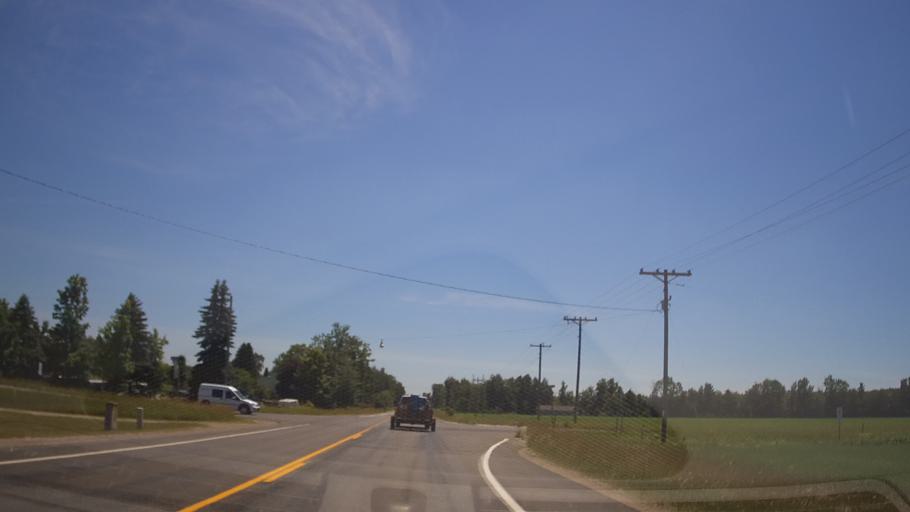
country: US
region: Michigan
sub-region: Grand Traverse County
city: Kingsley
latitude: 44.6001
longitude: -85.6964
